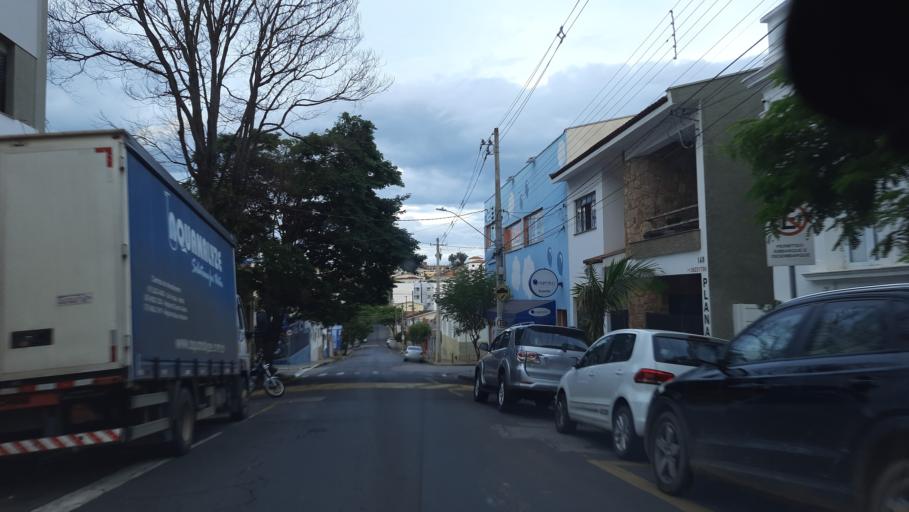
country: BR
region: Sao Paulo
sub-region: Sao Joao Da Boa Vista
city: Sao Joao da Boa Vista
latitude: -21.9680
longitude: -46.7953
